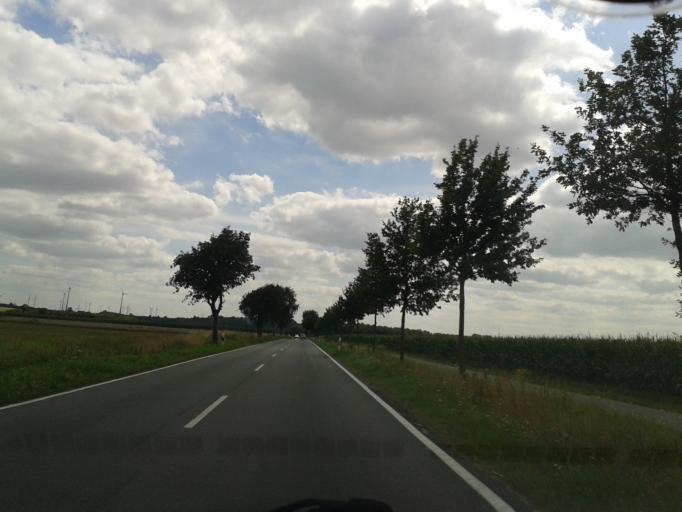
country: DE
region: North Rhine-Westphalia
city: Bad Lippspringe
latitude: 51.7659
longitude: 8.8363
